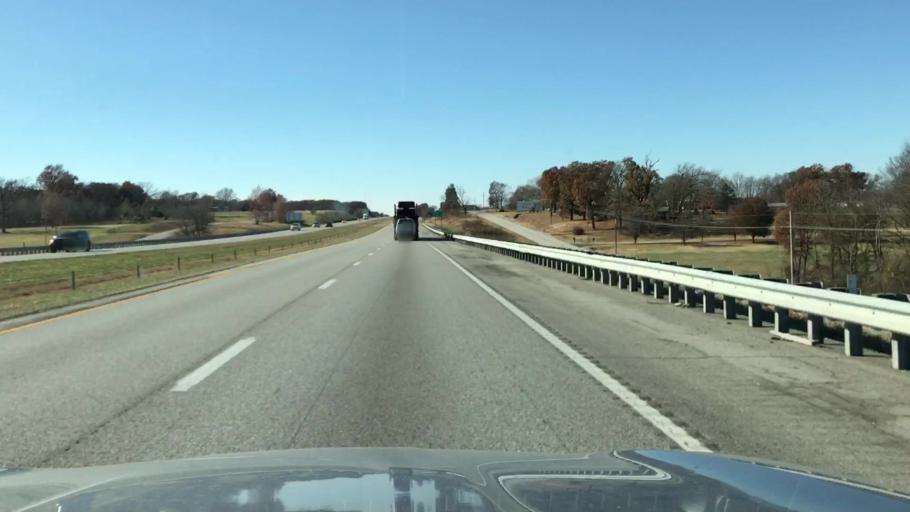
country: US
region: Missouri
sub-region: Jasper County
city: Duenweg
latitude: 37.0821
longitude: -94.3252
